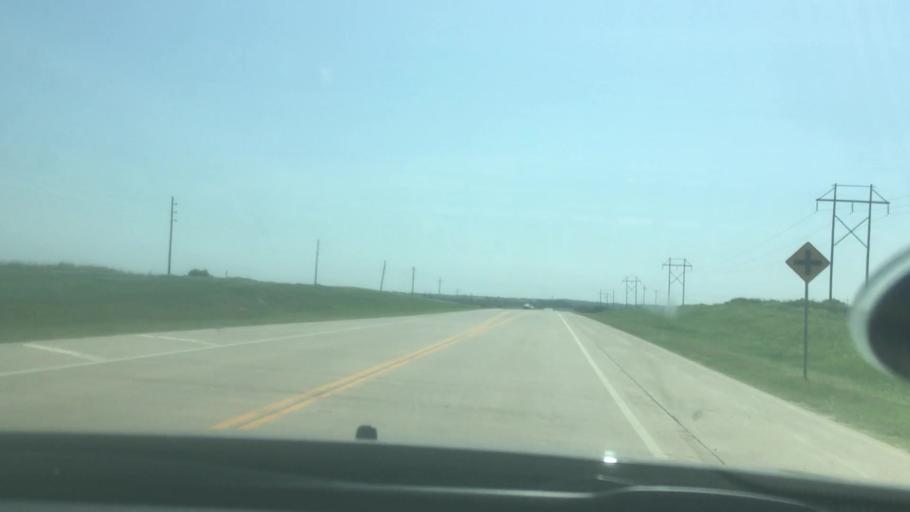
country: US
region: Oklahoma
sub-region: Garvin County
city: Stratford
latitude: 34.6520
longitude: -96.8307
